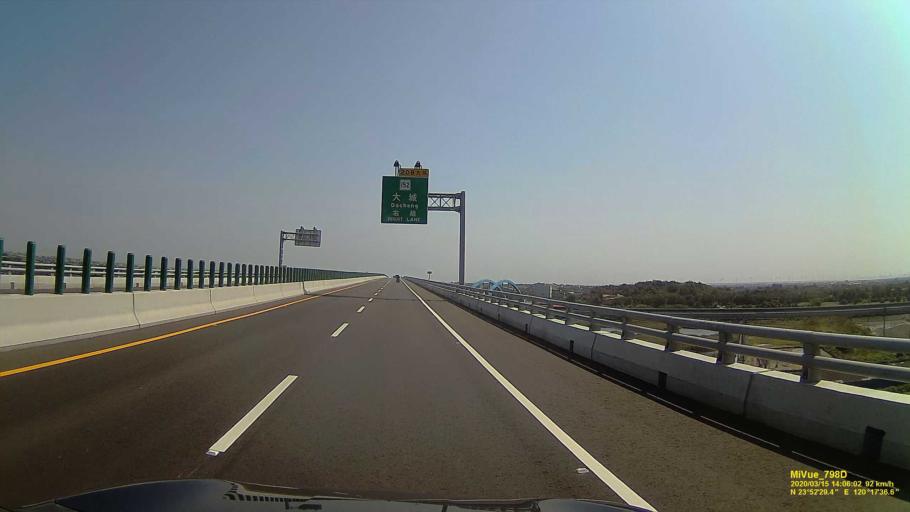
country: TW
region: Taiwan
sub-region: Yunlin
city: Douliu
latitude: 23.8743
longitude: 120.2936
